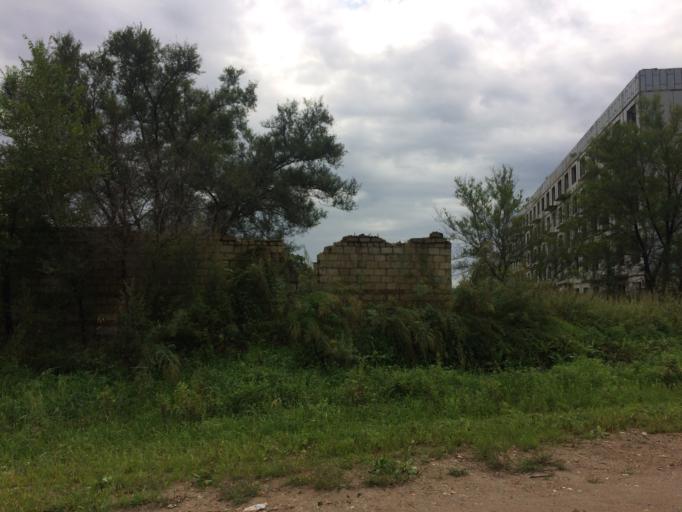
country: RU
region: Primorskiy
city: Lazo
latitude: 45.8242
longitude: 133.6430
